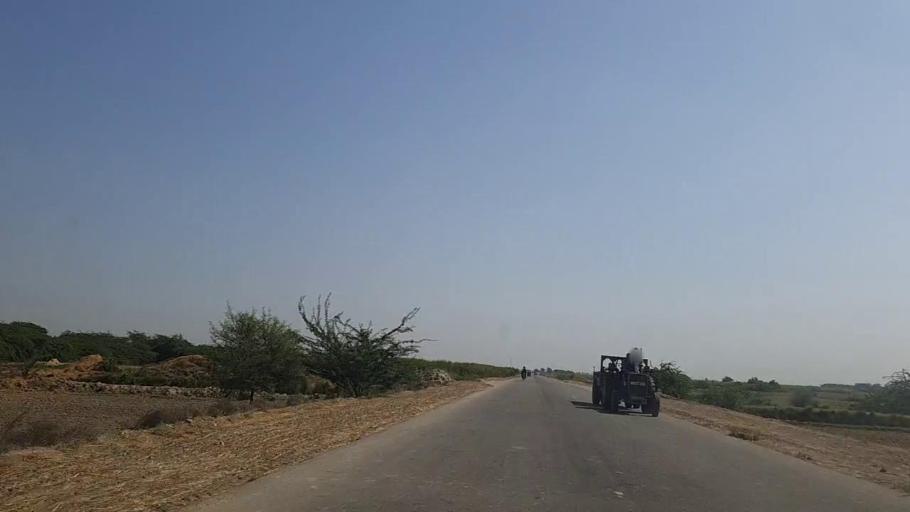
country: PK
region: Sindh
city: Mirpur Batoro
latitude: 24.7561
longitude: 68.2278
